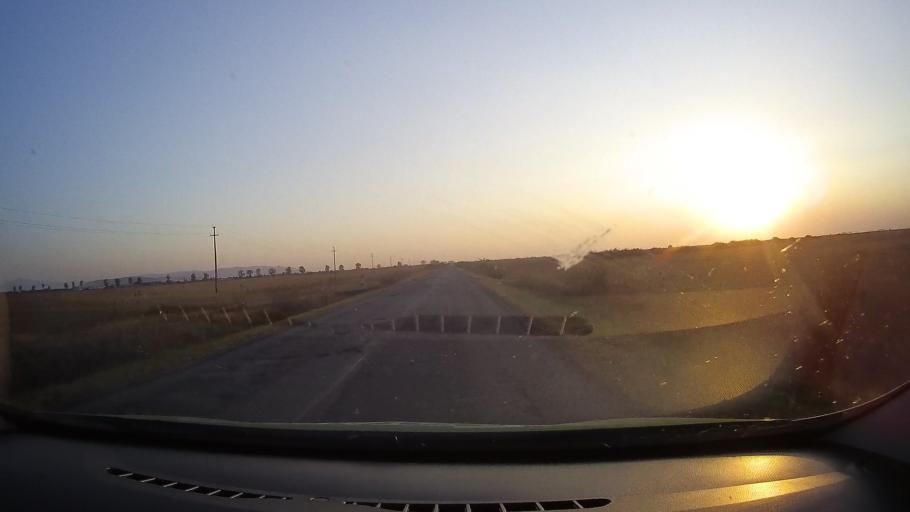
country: RO
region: Arad
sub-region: Comuna Seleus
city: Seleus
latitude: 46.4015
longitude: 21.7247
